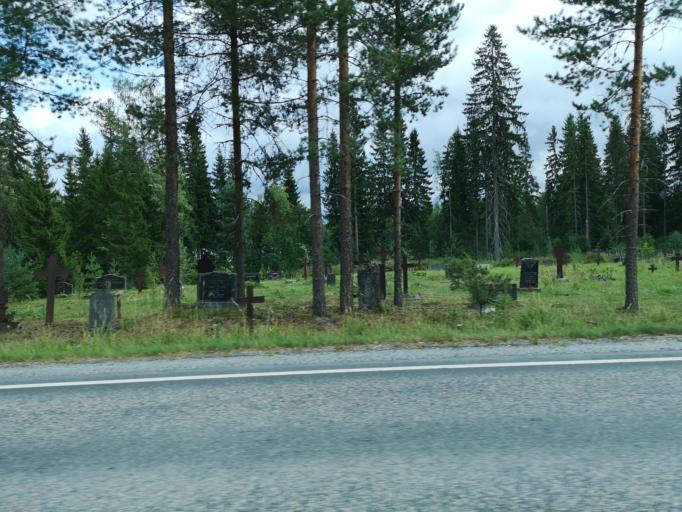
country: FI
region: Central Finland
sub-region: Jyvaeskylae
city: Hankasalmi
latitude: 62.3759
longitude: 26.4409
